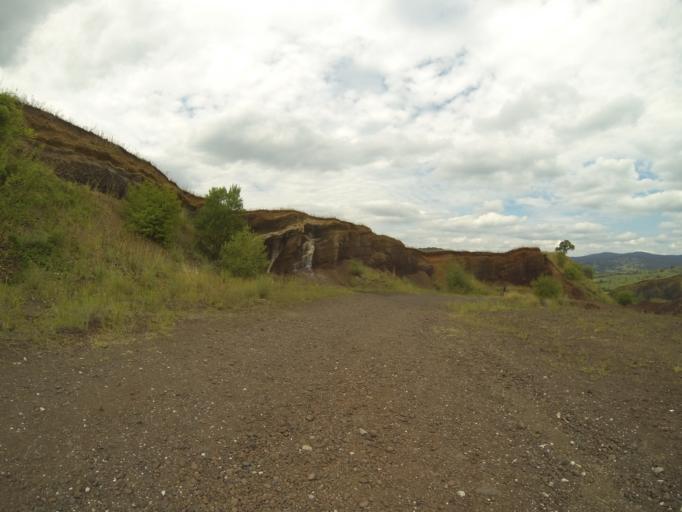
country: RO
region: Brasov
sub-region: Comuna Hoghiz
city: Hoghiz
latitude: 46.0313
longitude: 25.4169
